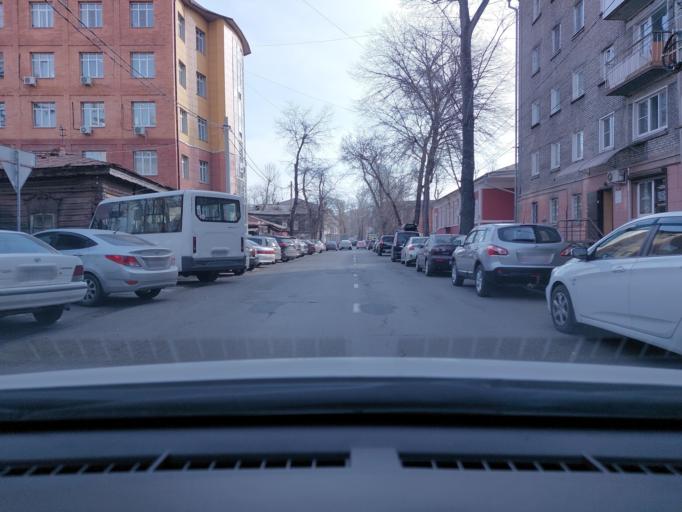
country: RU
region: Irkutsk
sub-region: Irkutskiy Rayon
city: Irkutsk
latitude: 52.2809
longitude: 104.2886
